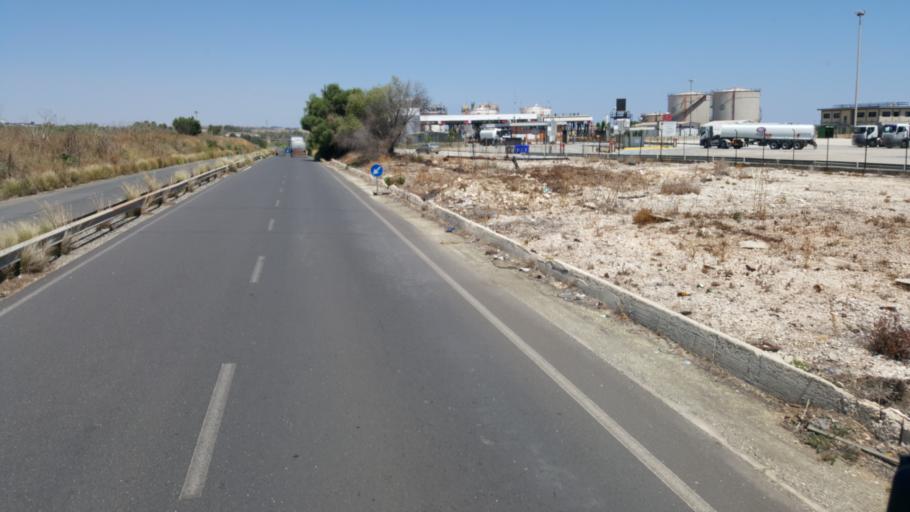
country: IT
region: Sicily
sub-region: Provincia di Siracusa
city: Melilli
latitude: 37.2049
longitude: 15.1598
